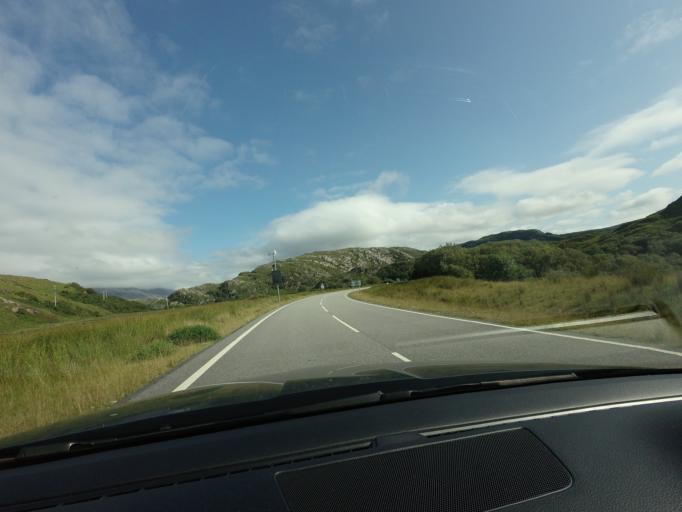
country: GB
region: Scotland
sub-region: Highland
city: Ullapool
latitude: 58.3772
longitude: -5.0183
